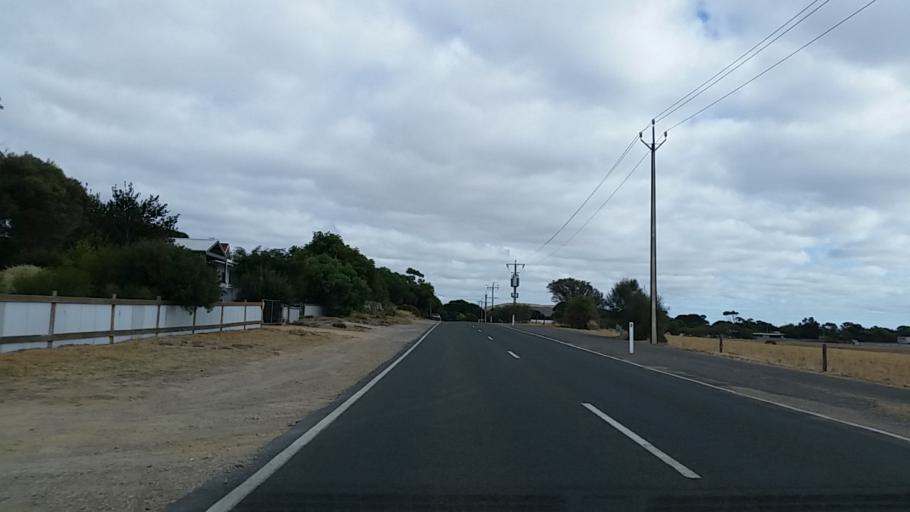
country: AU
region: South Australia
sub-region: Yankalilla
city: Normanville
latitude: -35.4416
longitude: 138.3175
